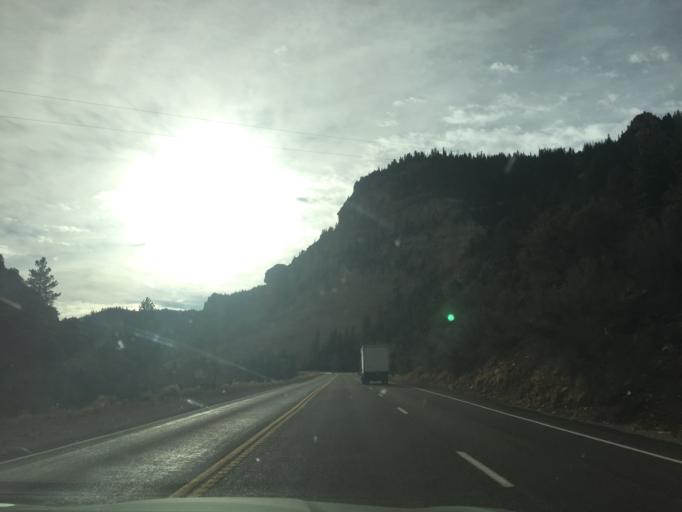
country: US
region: Utah
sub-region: Iron County
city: Cedar City
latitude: 37.6390
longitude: -112.9517
